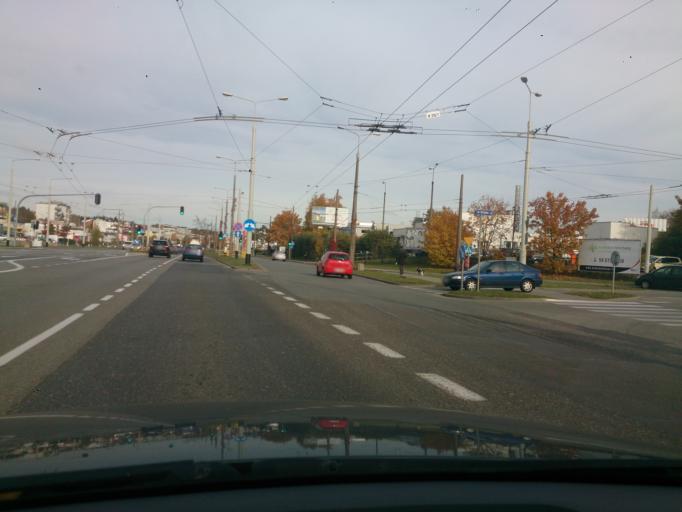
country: PL
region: Pomeranian Voivodeship
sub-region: Gdynia
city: Wielki Kack
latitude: 54.4726
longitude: 18.5137
